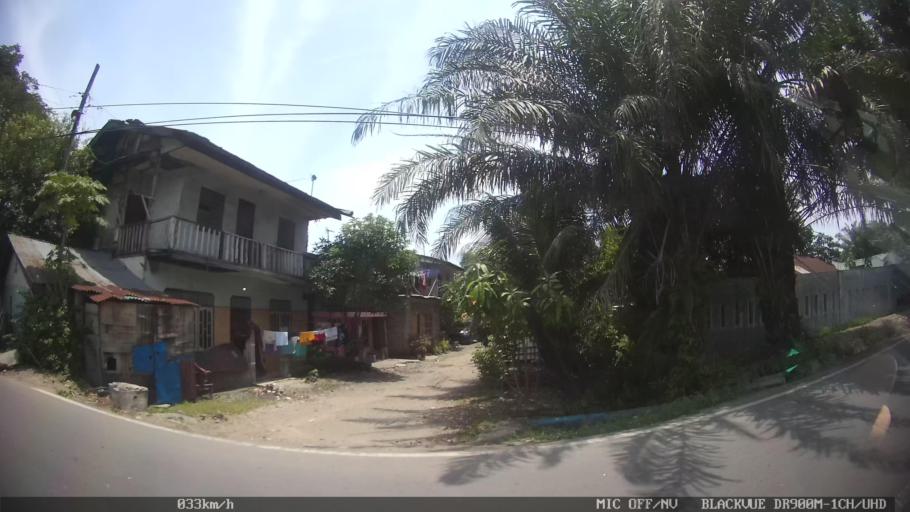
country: ID
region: North Sumatra
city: Labuhan Deli
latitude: 3.7363
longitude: 98.6765
